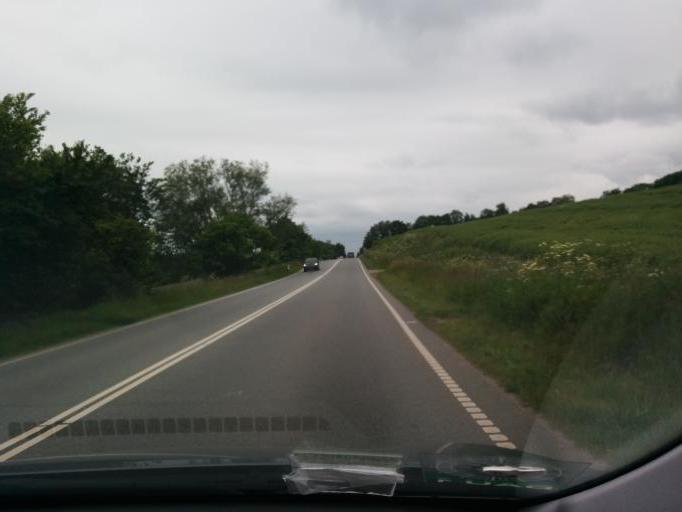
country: DK
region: Central Jutland
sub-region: Syddjurs Kommune
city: Ronde
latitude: 56.3041
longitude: 10.3979
